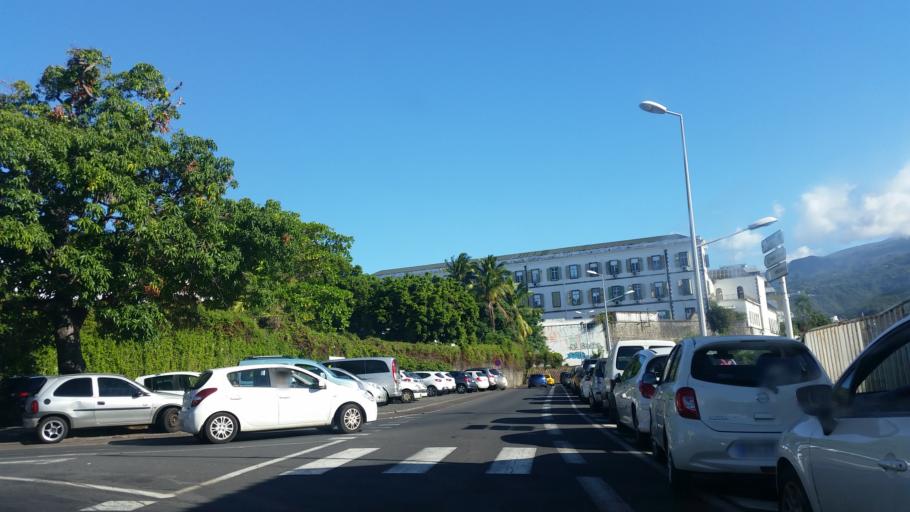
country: RE
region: Reunion
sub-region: Reunion
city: Saint-Denis
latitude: -20.8769
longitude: 55.4466
